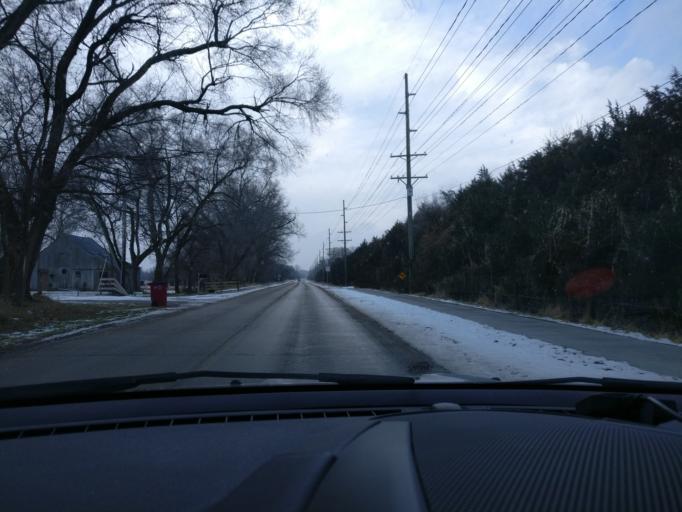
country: US
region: Nebraska
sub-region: Dodge County
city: Fremont
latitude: 41.4362
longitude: -96.5216
